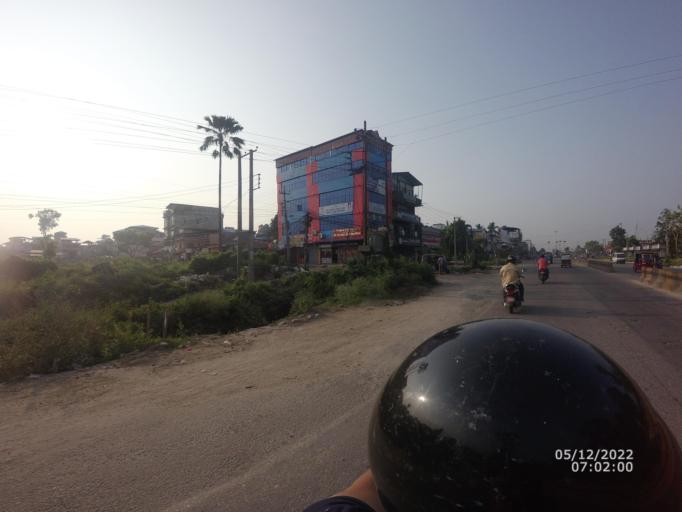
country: NP
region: Central Region
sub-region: Narayani Zone
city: Bharatpur
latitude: 27.6834
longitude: 84.4300
